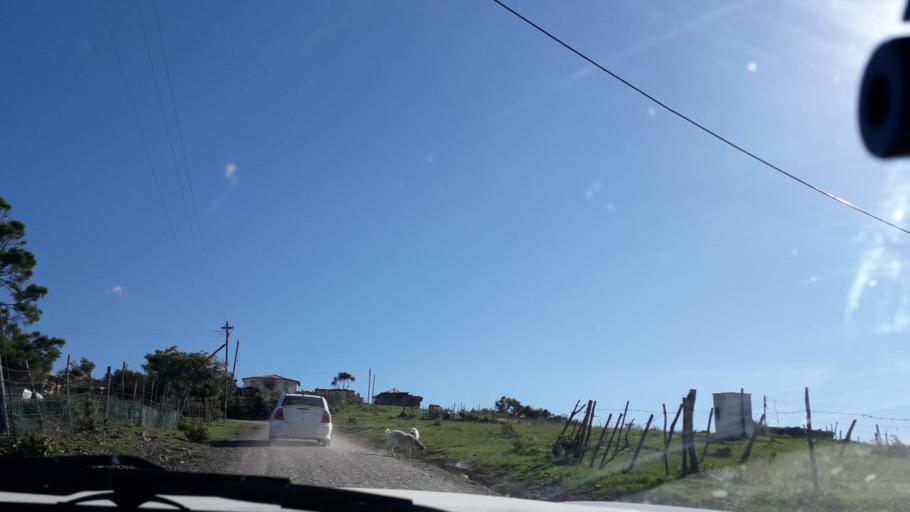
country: ZA
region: Eastern Cape
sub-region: Buffalo City Metropolitan Municipality
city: East London
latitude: -32.7996
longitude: 27.9623
